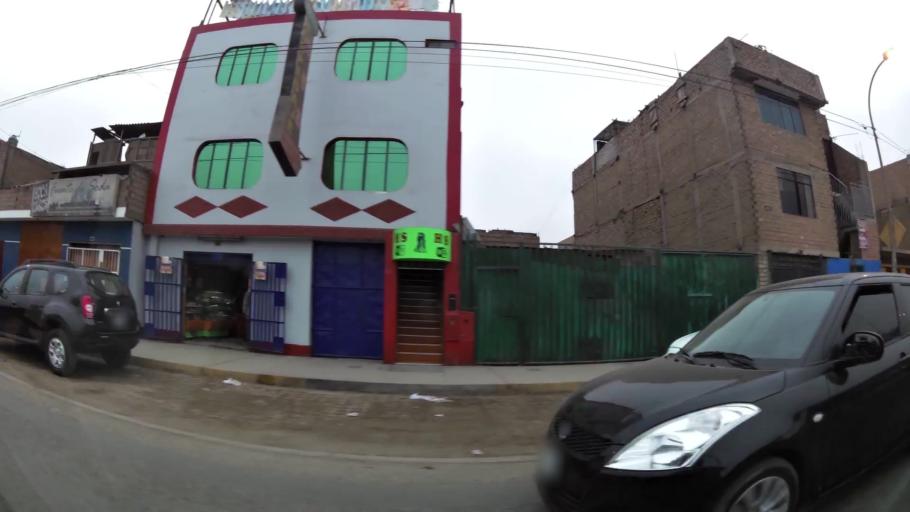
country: PE
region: Lima
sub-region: Lima
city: Urb. Santo Domingo
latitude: -11.9157
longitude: -77.0468
